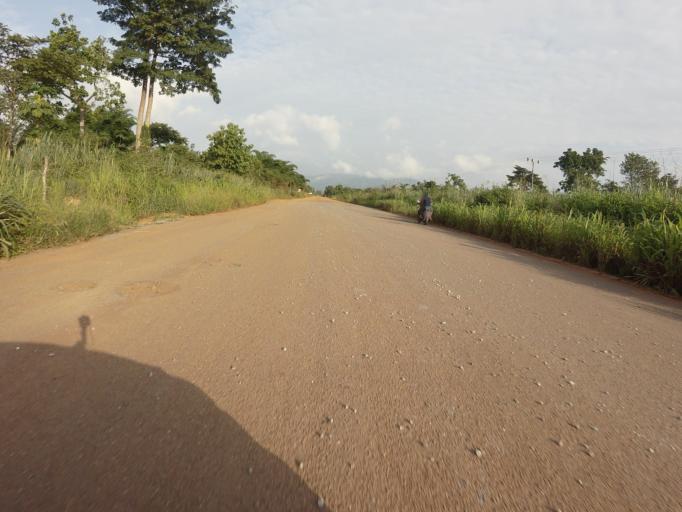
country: GH
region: Volta
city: Kpandu
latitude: 6.9703
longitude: 0.4536
